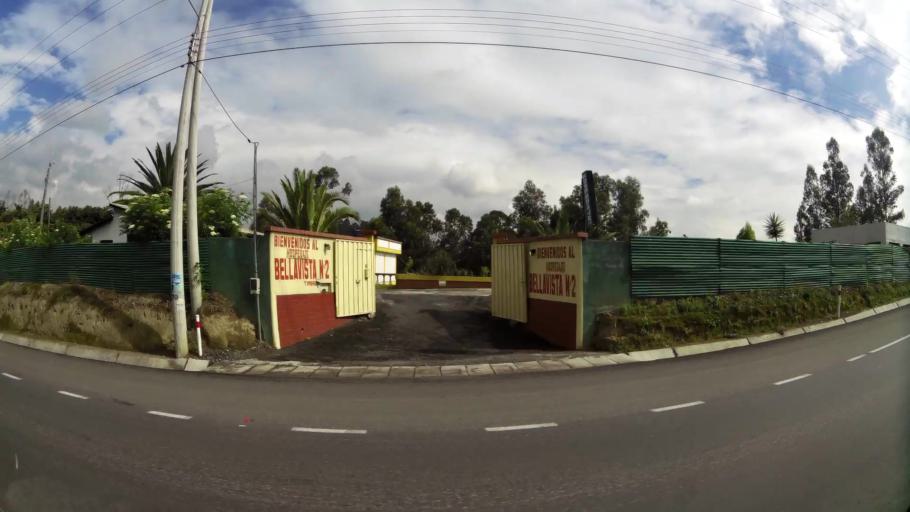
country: EC
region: Pichincha
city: Sangolqui
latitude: -0.3266
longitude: -78.4195
